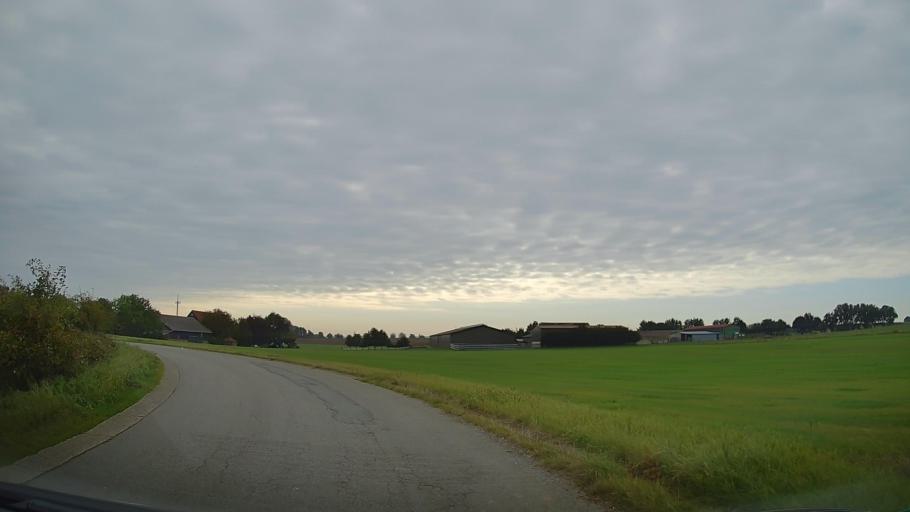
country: DE
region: Schleswig-Holstein
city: Hohenfelde
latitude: 54.3751
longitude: 10.5418
